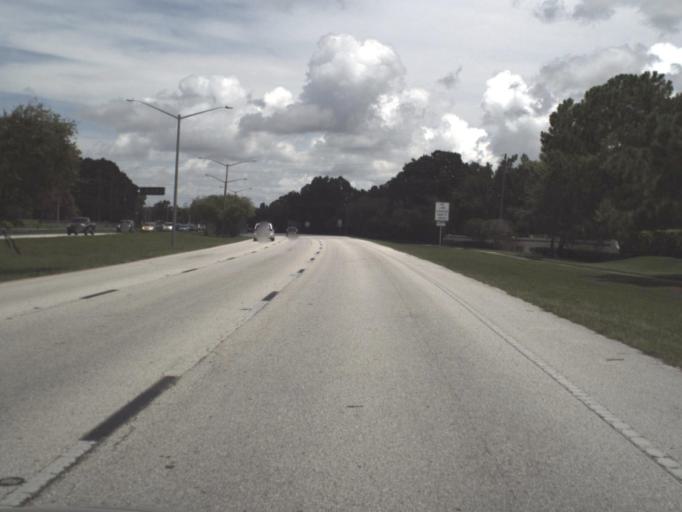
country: US
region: Florida
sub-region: Pinellas County
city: East Lake
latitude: 28.0832
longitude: -82.7006
